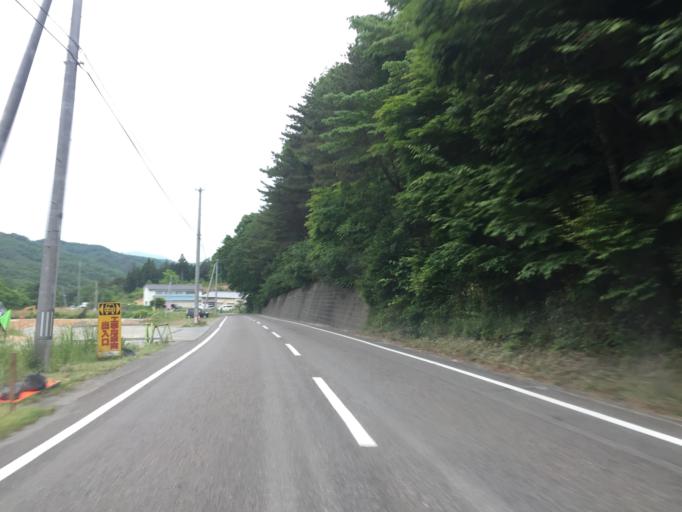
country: JP
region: Fukushima
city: Namie
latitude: 37.4102
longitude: 140.8462
